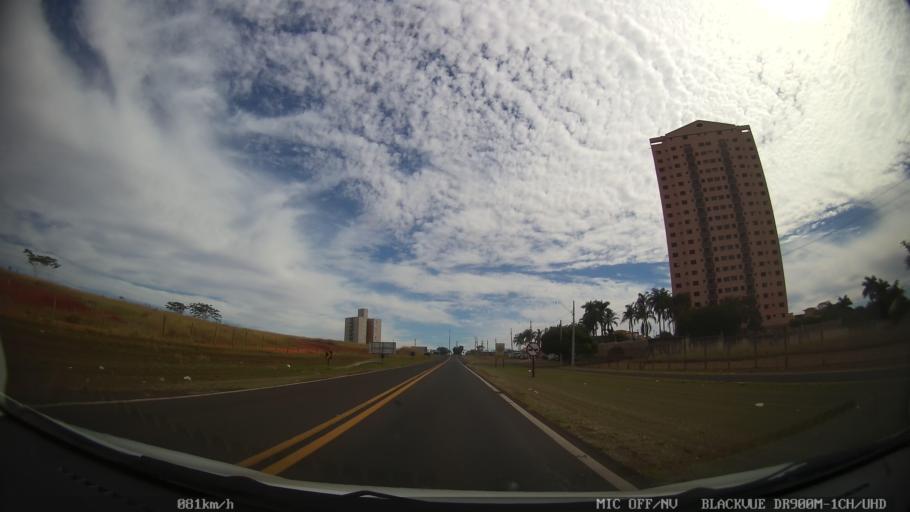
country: BR
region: Sao Paulo
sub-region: Catanduva
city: Catanduva
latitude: -21.1522
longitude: -48.9575
